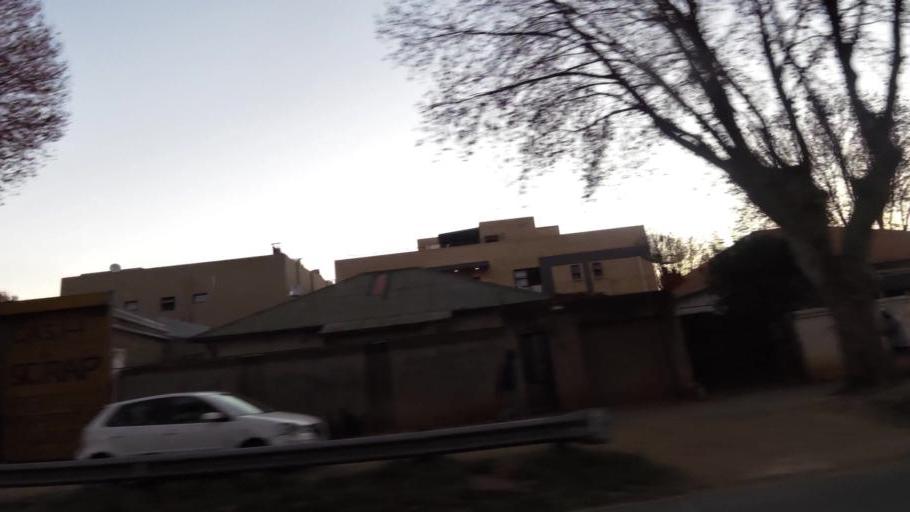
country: ZA
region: Gauteng
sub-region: City of Johannesburg Metropolitan Municipality
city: Johannesburg
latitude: -26.2074
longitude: 28.0113
